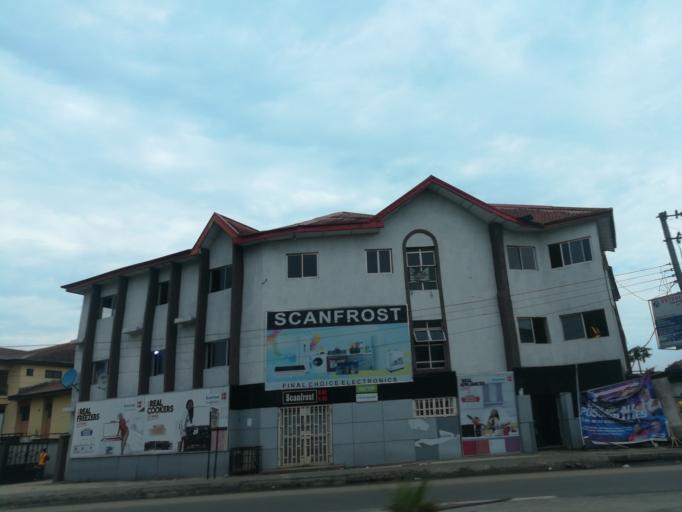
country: NG
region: Rivers
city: Port Harcourt
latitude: 4.8458
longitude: 6.9751
